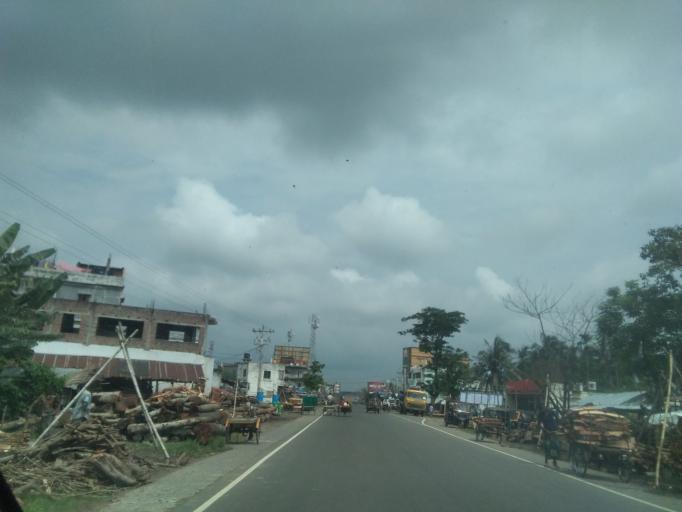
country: BD
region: Khulna
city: Kesabpur
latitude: 22.8392
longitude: 89.2986
